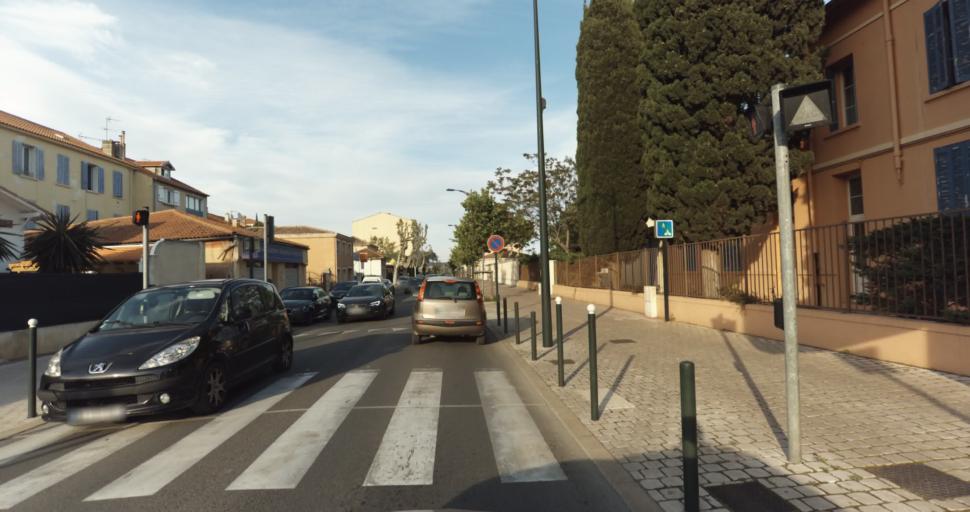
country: FR
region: Provence-Alpes-Cote d'Azur
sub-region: Departement du Var
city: Hyeres
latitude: 43.1221
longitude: 6.1415
